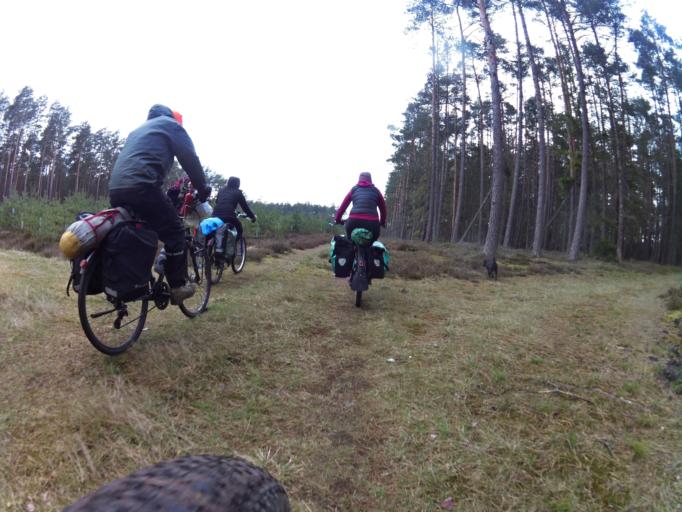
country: PL
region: Pomeranian Voivodeship
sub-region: Powiat slupski
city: Kepice
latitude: 54.3106
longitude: 16.8251
